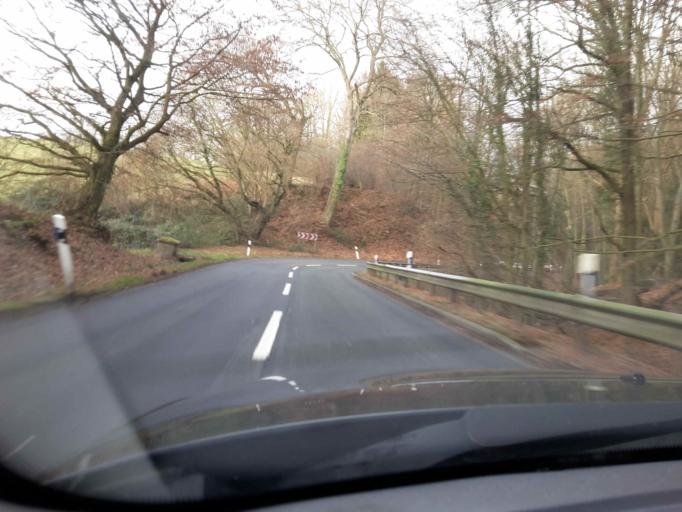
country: DE
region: North Rhine-Westphalia
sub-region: Regierungsbezirk Koln
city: Hennef
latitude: 50.7540
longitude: 7.2718
